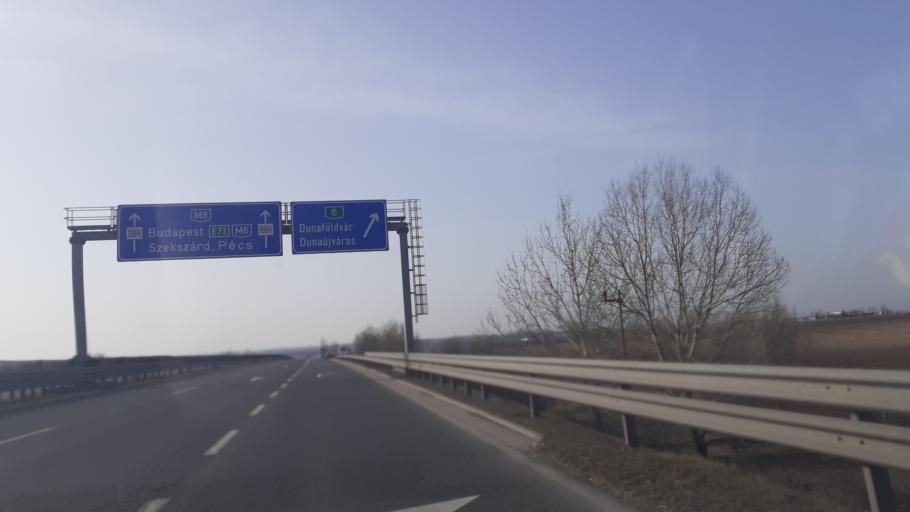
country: HU
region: Bacs-Kiskun
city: Apostag
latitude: 46.9087
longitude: 18.9385
